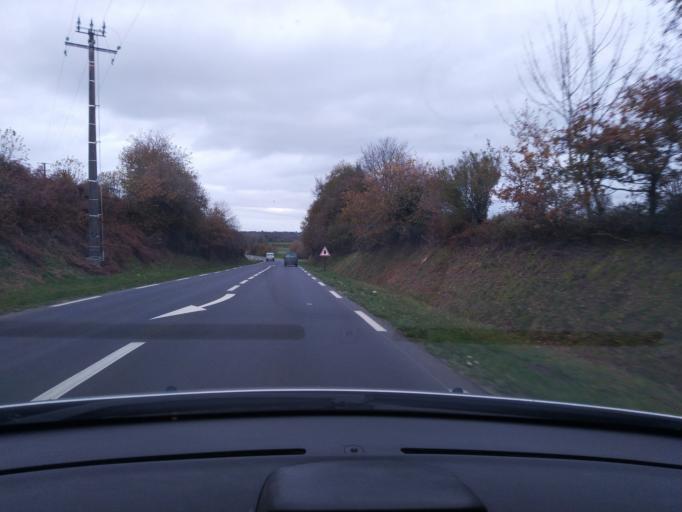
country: FR
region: Brittany
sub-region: Departement des Cotes-d'Armor
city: Plounevez-Moedec
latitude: 48.5645
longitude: -3.4972
